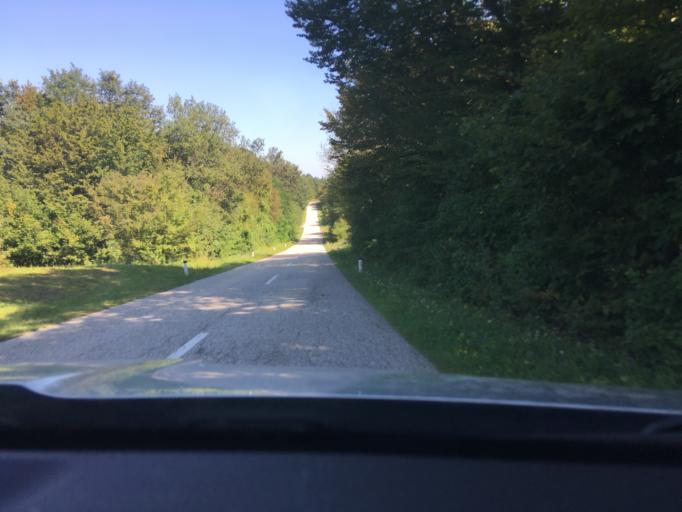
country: SI
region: Metlika
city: Metlika
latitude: 45.5007
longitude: 15.3434
